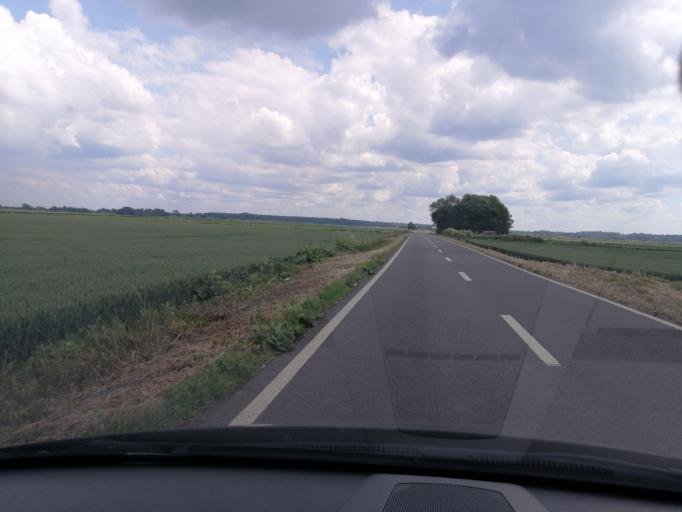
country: GB
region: England
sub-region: Cambridgeshire
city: Yaxley
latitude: 52.5067
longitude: -0.2573
